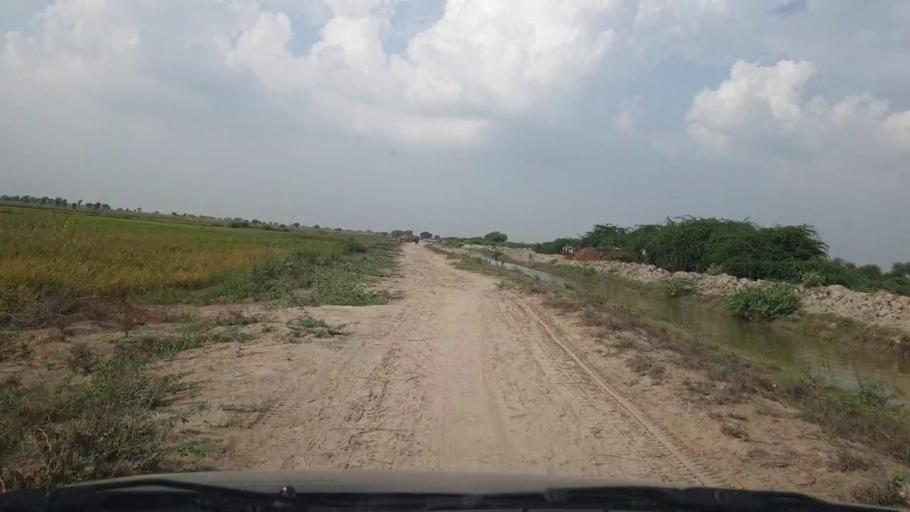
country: PK
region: Sindh
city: Badin
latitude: 24.5686
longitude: 68.6340
